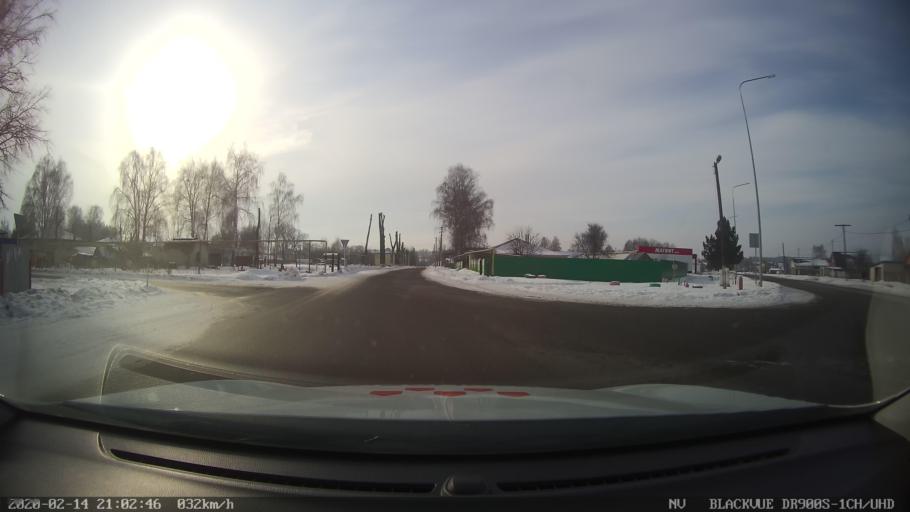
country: RU
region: Tatarstan
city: Kuybyshevskiy Zaton
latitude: 55.1594
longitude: 49.1779
